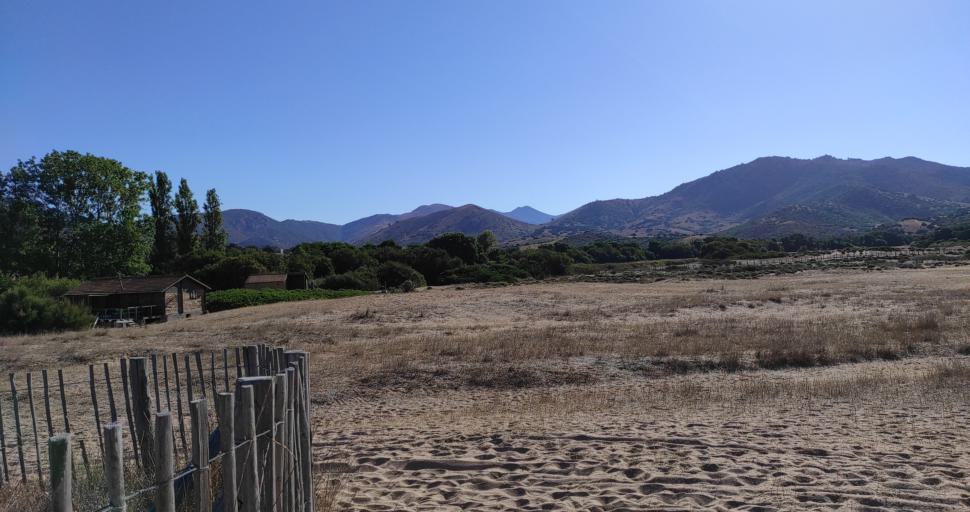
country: FR
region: Corsica
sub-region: Departement de la Corse-du-Sud
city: Alata
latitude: 41.9898
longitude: 8.6704
